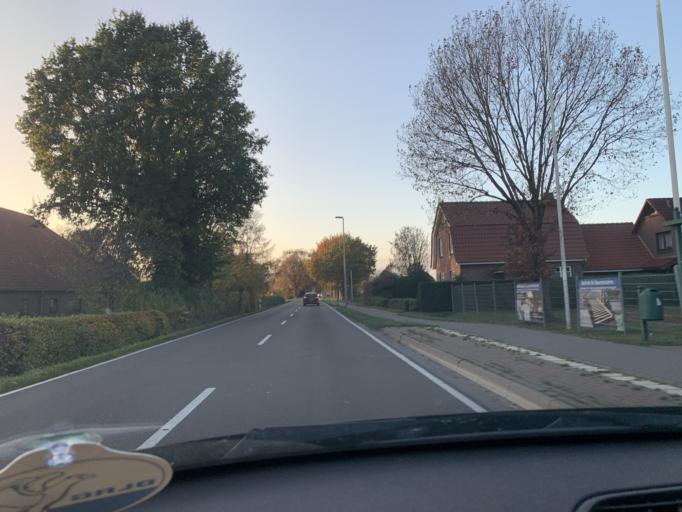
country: DE
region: Lower Saxony
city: Edewecht
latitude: 53.1220
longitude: 8.0165
